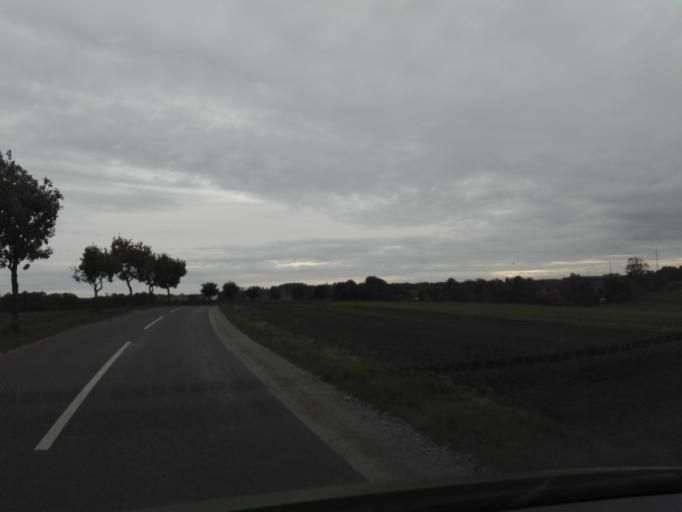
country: DK
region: Central Jutland
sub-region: Arhus Kommune
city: Solbjerg
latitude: 56.0670
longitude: 10.0816
